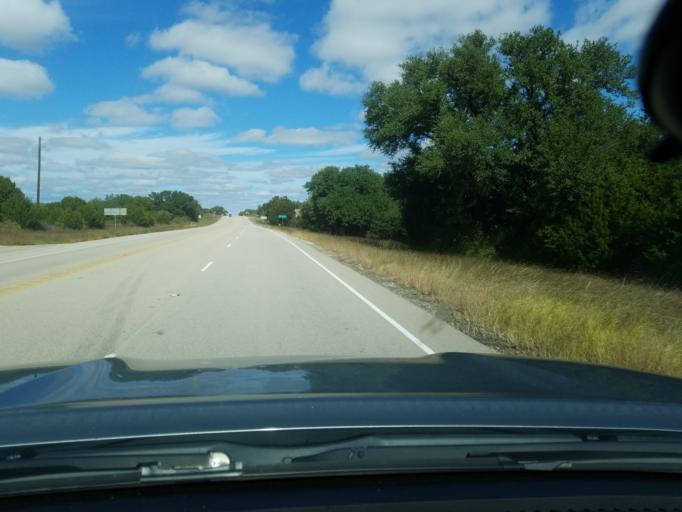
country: US
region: Texas
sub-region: Hamilton County
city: Hamilton
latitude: 31.5893
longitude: -98.1567
